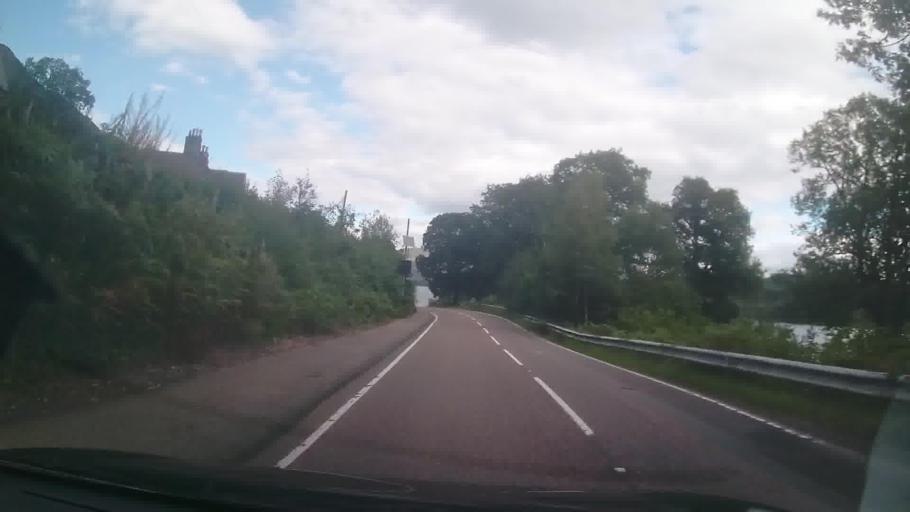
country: GB
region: Scotland
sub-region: Argyll and Bute
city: Garelochhead
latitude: 56.3967
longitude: -5.0545
